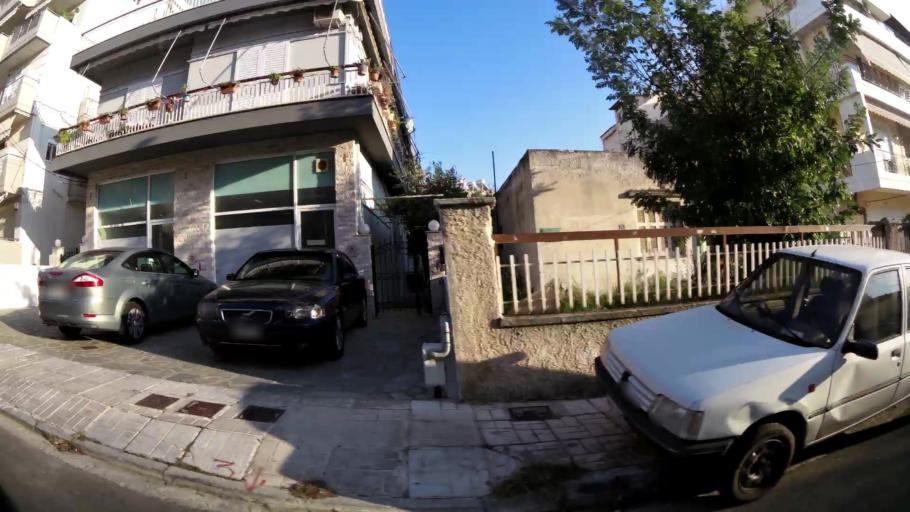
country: GR
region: Attica
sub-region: Nomarchia Athinas
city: Argyroupoli
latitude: 37.8974
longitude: 23.7680
